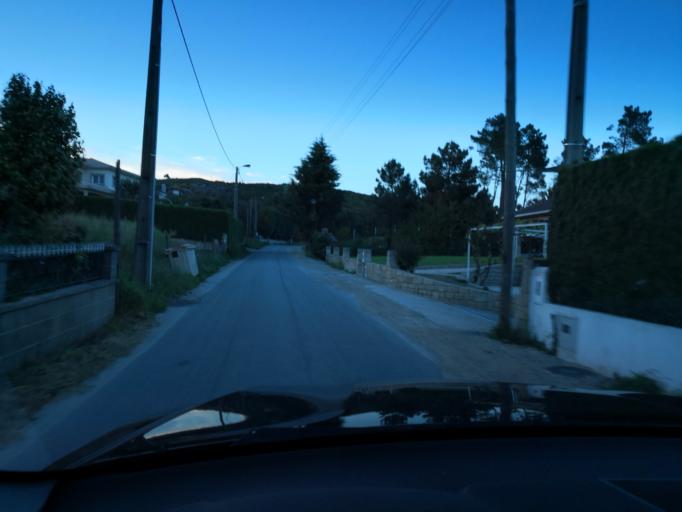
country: PT
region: Vila Real
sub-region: Vila Real
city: Vila Real
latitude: 41.3383
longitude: -7.6985
